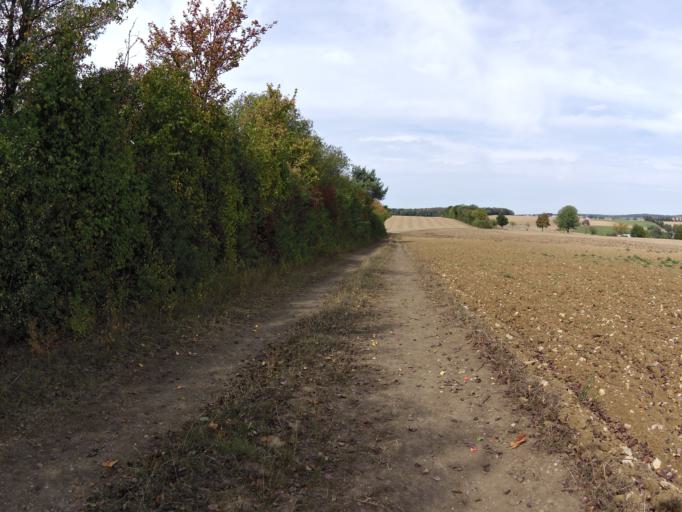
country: DE
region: Bavaria
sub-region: Regierungsbezirk Unterfranken
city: Waldbuttelbrunn
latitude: 49.7796
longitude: 9.8299
